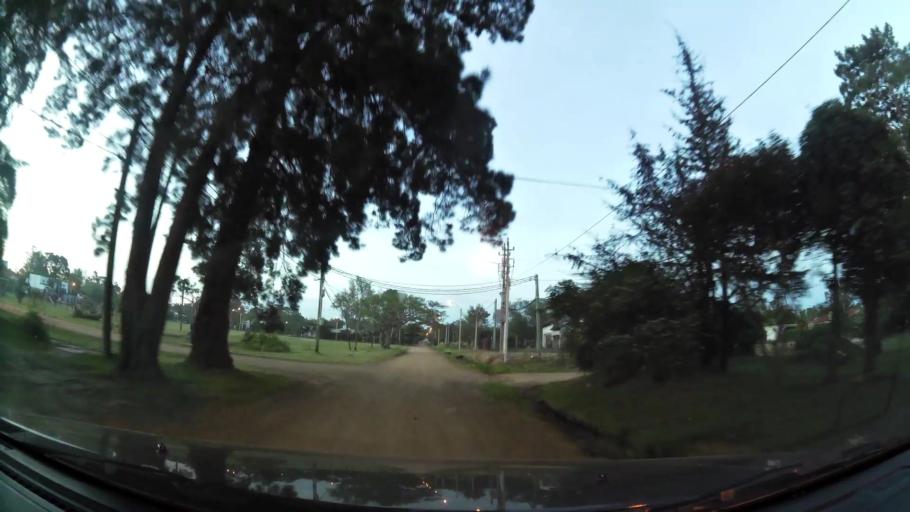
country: UY
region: Canelones
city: Atlantida
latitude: -34.7749
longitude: -55.7486
